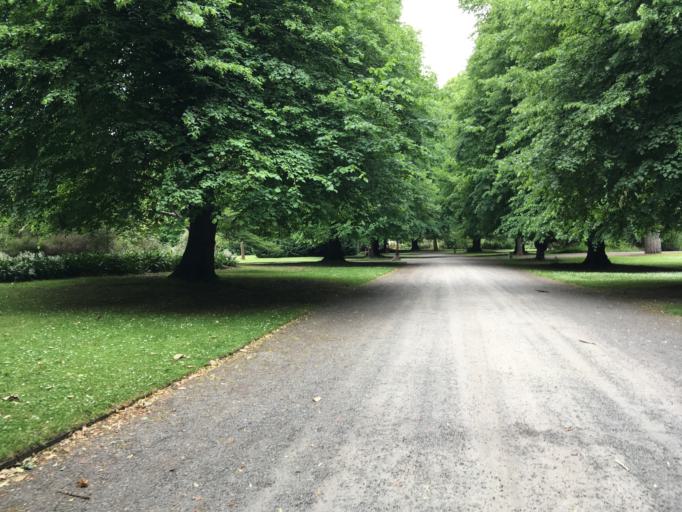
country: NZ
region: Canterbury
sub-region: Christchurch City
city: Christchurch
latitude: -43.5309
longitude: 172.6202
